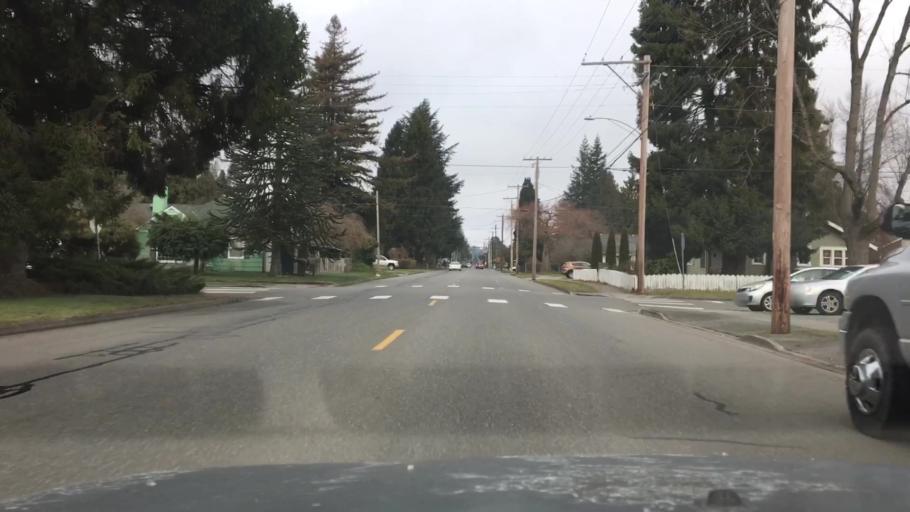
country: US
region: Washington
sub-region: Skagit County
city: Sedro-Woolley
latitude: 48.5012
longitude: -122.2259
